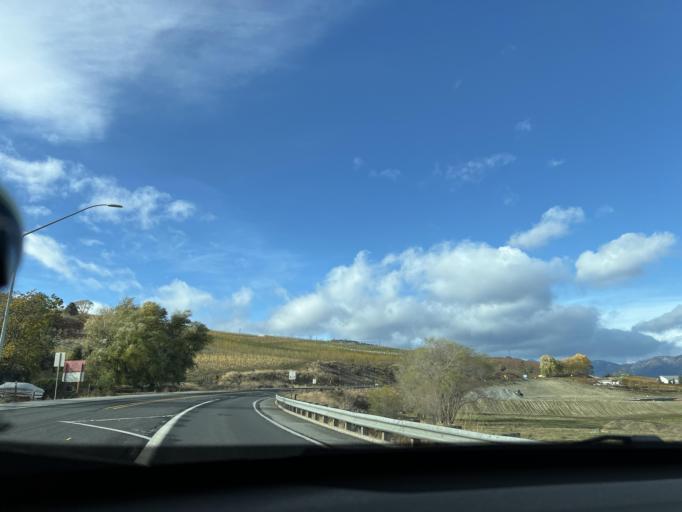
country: US
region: Washington
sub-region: Chelan County
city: Chelan
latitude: 47.8392
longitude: -120.0927
